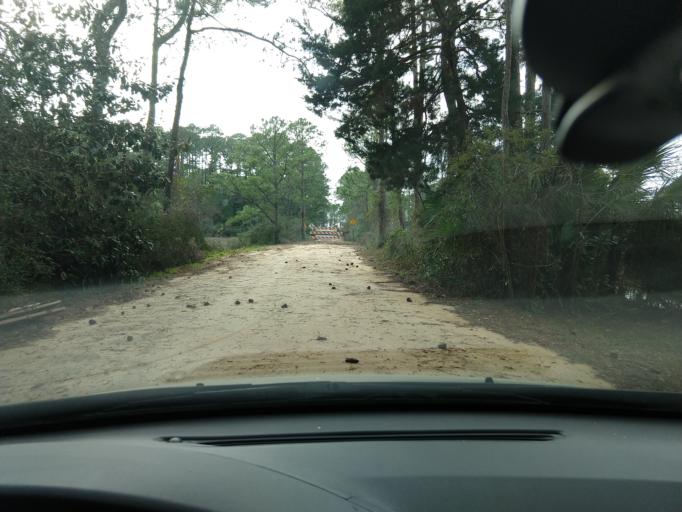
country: US
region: Florida
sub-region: Walton County
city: Seaside
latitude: 30.3961
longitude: -86.2298
